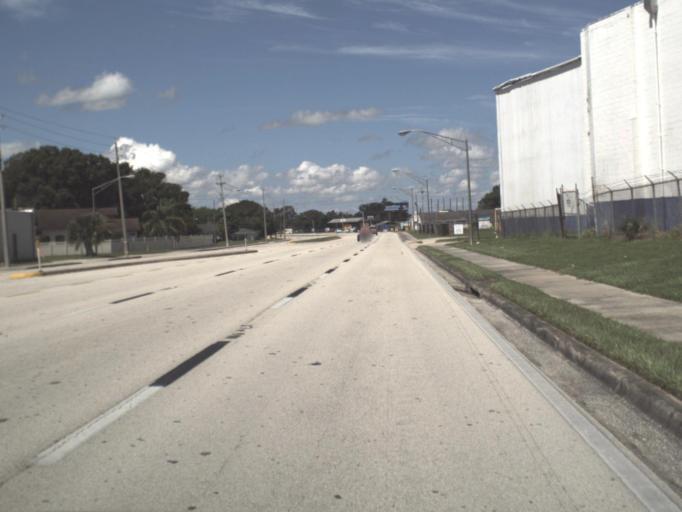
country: US
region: Florida
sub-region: Polk County
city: Auburndale
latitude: 28.0604
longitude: -81.8001
